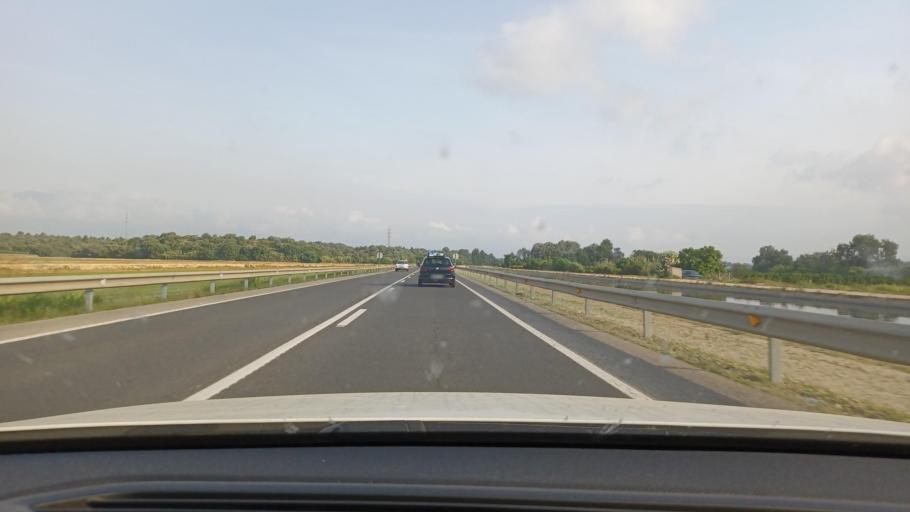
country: ES
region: Catalonia
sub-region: Provincia de Tarragona
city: Masdenverge
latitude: 40.7566
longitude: 0.5383
